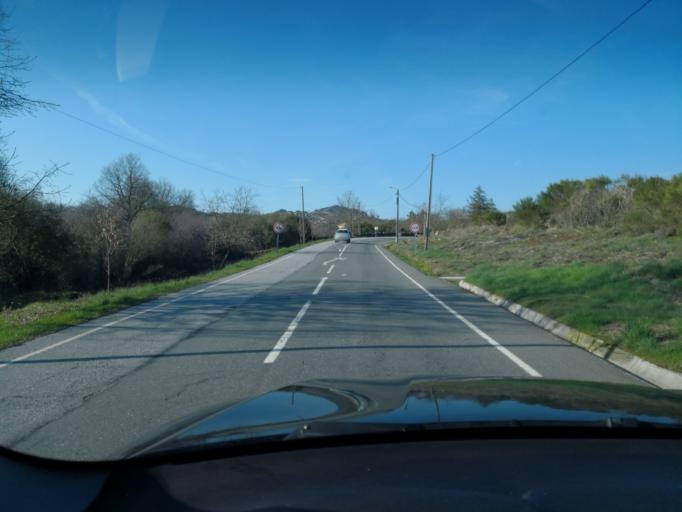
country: PT
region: Vila Real
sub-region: Sabrosa
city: Sabrosa
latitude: 41.3606
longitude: -7.6431
